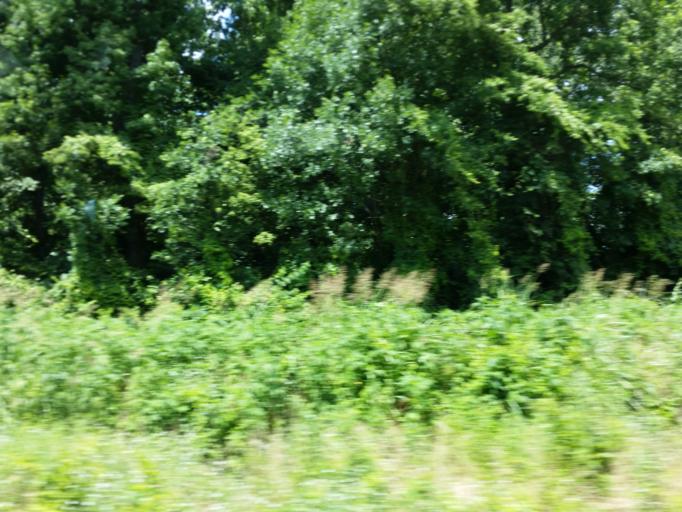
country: US
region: Tennessee
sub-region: Lake County
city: Tiptonville
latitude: 36.4940
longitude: -89.3648
